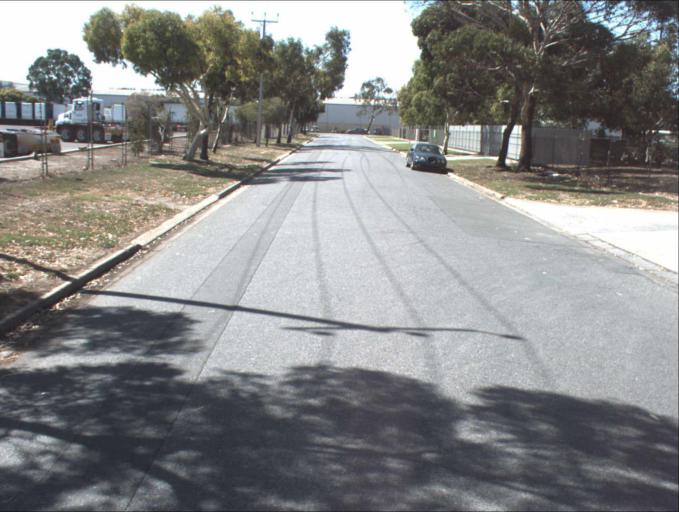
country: AU
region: South Australia
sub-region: Charles Sturt
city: Woodville North
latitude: -34.8426
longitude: 138.5550
